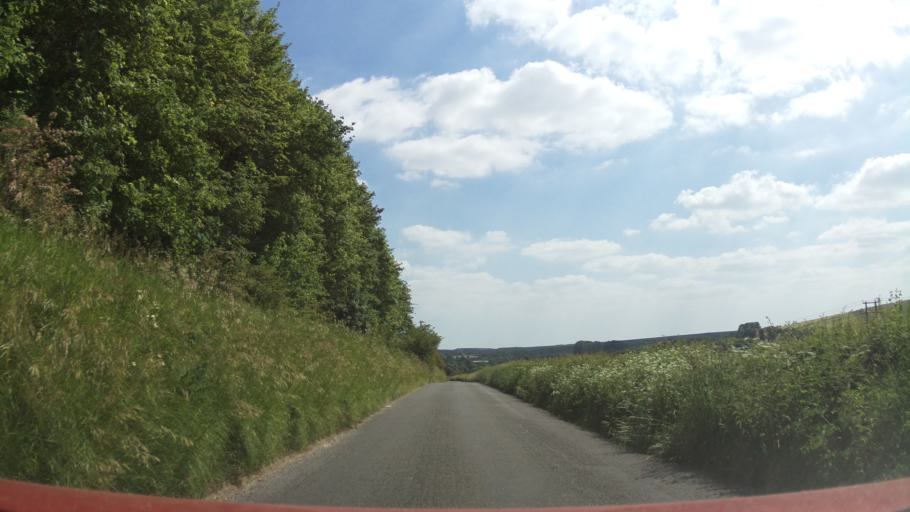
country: GB
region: England
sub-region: Wiltshire
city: Rushall
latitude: 51.2817
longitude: -1.8021
